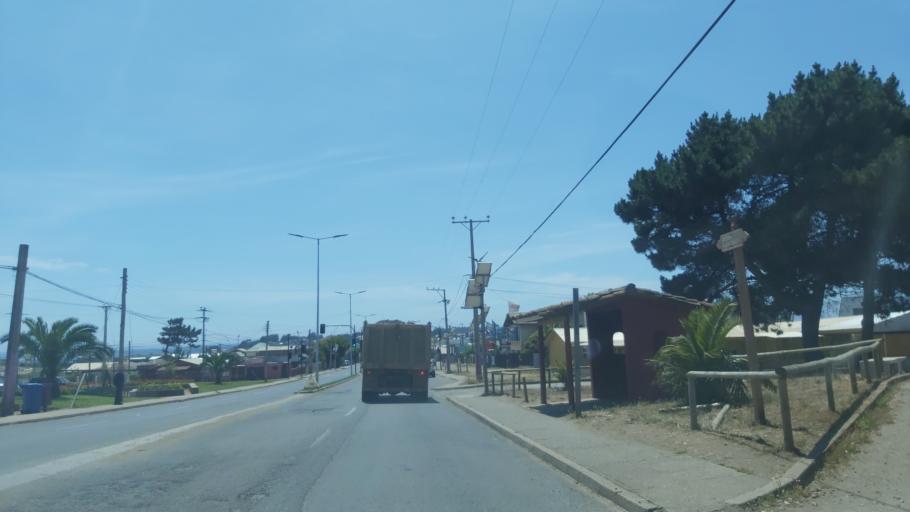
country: CL
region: Maule
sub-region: Provincia de Cauquenes
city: Cauquenes
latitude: -35.8119
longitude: -72.5725
